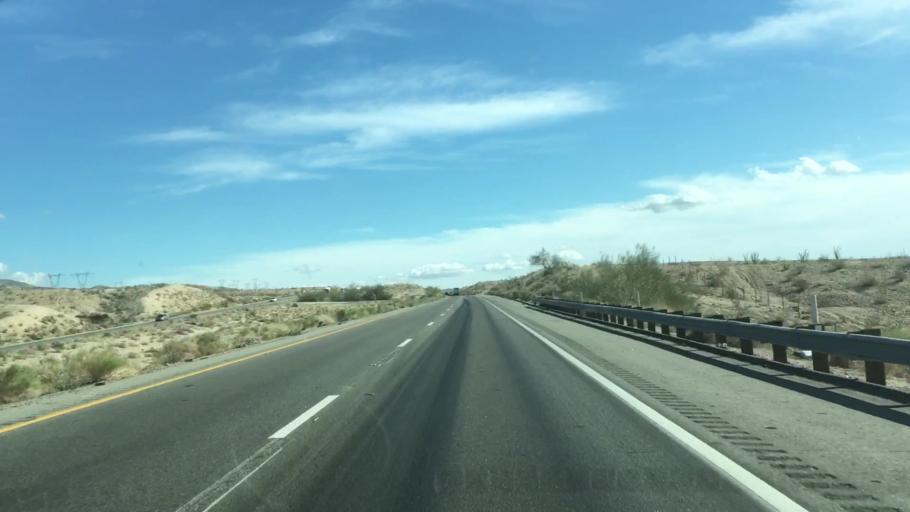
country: US
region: California
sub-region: Riverside County
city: Thermal
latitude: 33.6861
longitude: -116.0276
